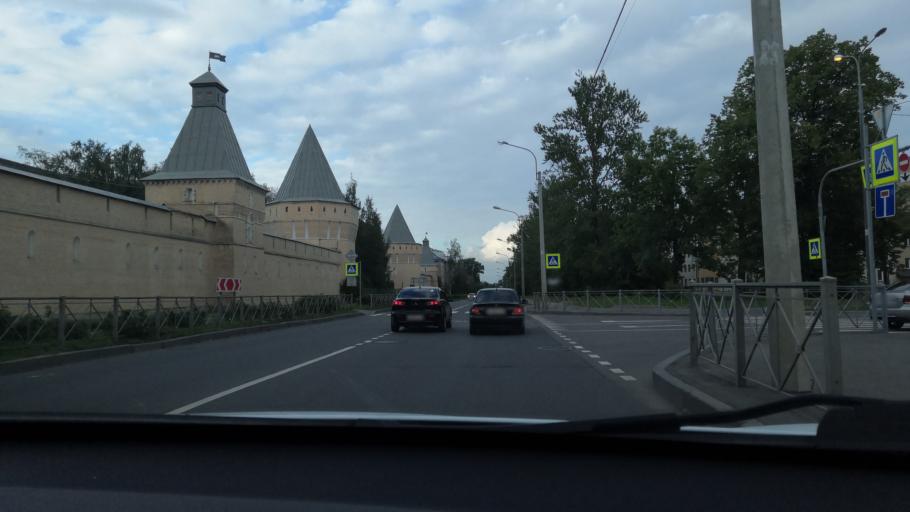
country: RU
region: St.-Petersburg
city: Pushkin
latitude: 59.7016
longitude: 30.4000
